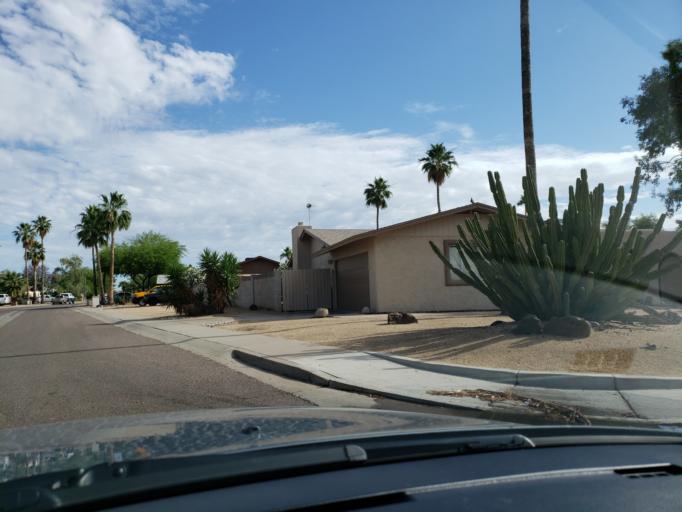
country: US
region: Arizona
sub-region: Maricopa County
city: Paradise Valley
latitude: 33.6154
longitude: -112.0082
